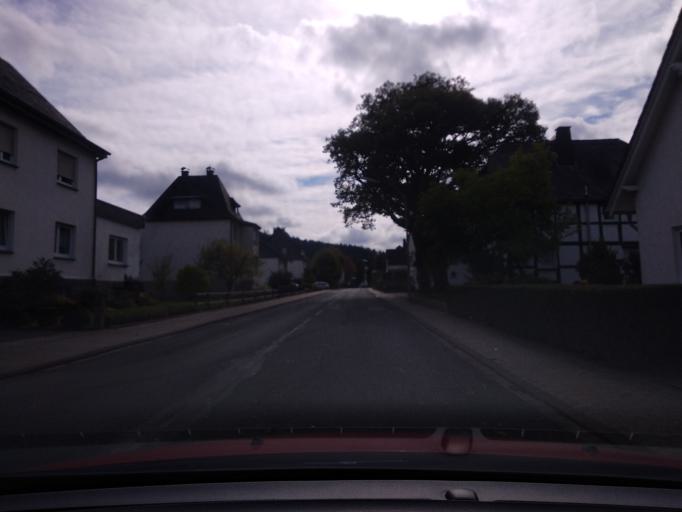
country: DE
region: North Rhine-Westphalia
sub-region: Regierungsbezirk Arnsberg
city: Bestwig
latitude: 51.3363
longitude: 8.4059
